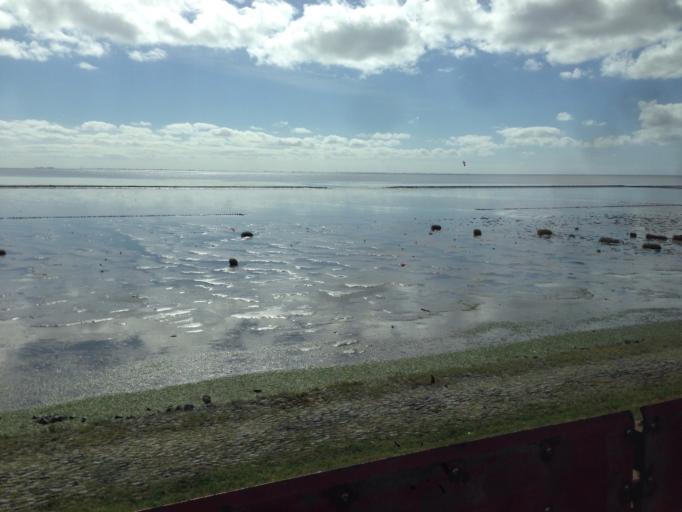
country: DE
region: Schleswig-Holstein
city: Friedrich-Wilhelm-Lubke-Koog
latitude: 54.8852
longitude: 8.5710
